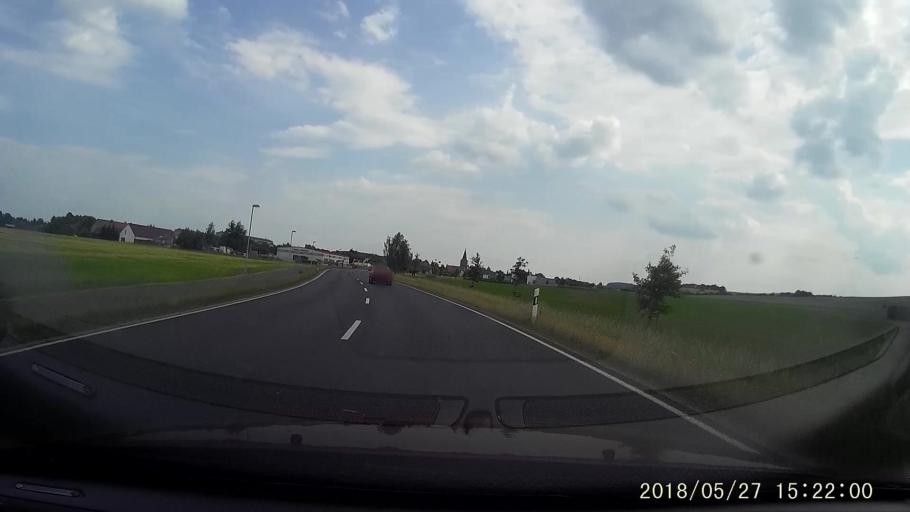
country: DE
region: Saxony
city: Kodersdorf
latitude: 51.2369
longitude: 14.8901
